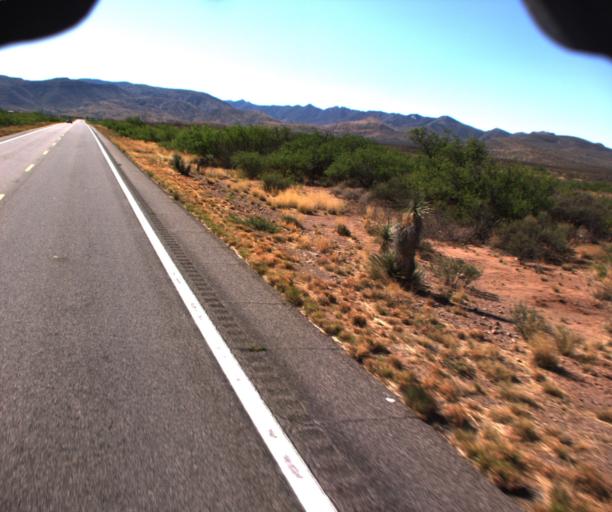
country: US
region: Arizona
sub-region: Cochise County
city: Bisbee
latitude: 31.5576
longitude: -110.0187
